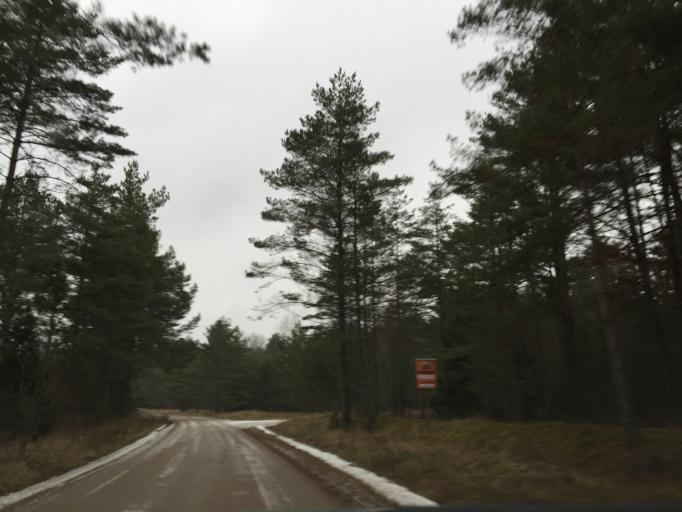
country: EE
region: Saare
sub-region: Kuressaare linn
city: Kuressaare
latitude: 58.4494
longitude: 22.2461
